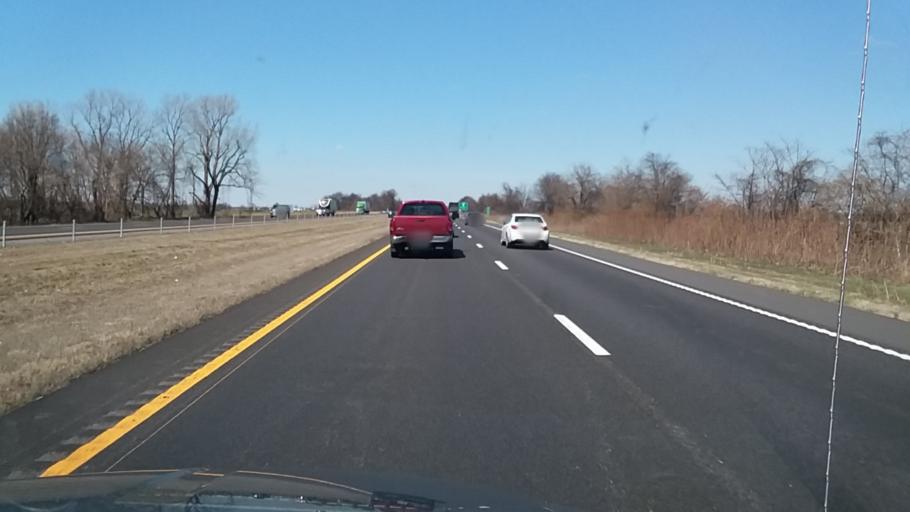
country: US
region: Missouri
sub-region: Scott County
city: Sikeston
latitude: 36.7380
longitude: -89.5377
